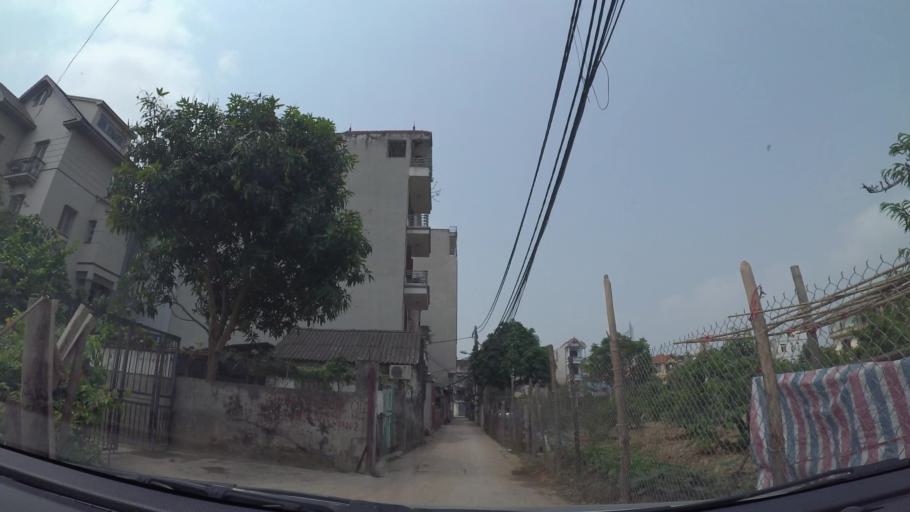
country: VN
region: Ha Noi
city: Tay Ho
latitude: 21.0867
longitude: 105.8002
